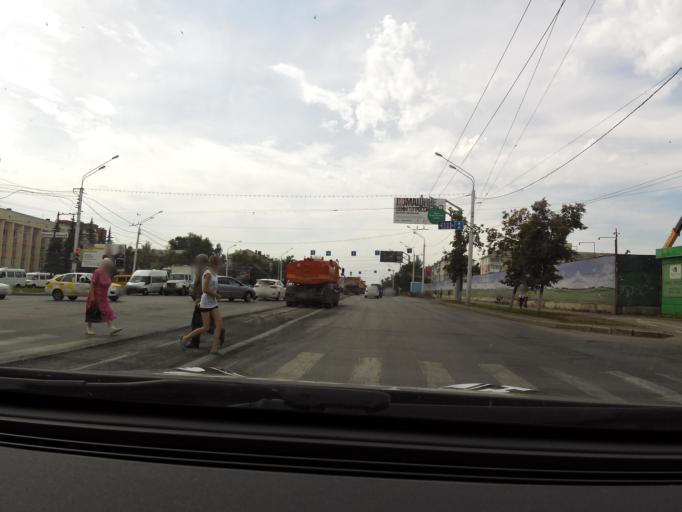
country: RU
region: Bashkortostan
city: Ufa
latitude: 54.7835
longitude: 56.0329
